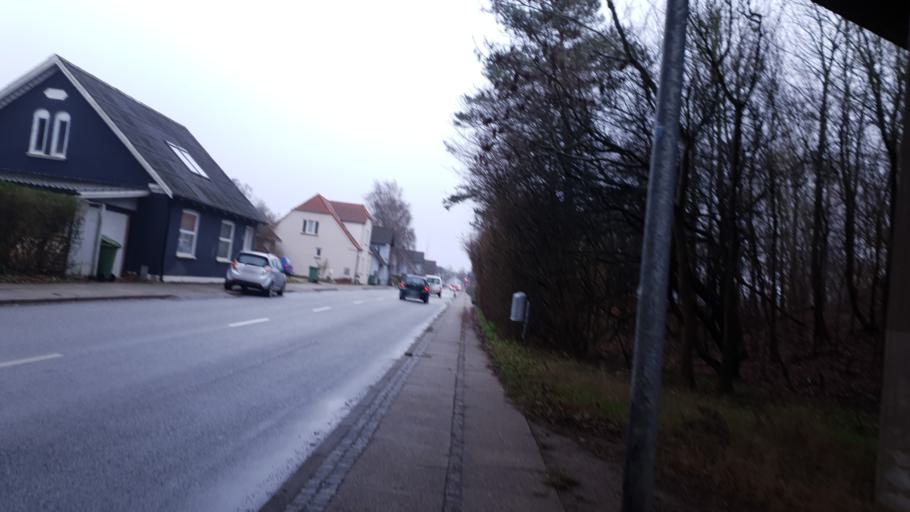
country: DK
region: Central Jutland
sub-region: Hedensted Kommune
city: Hedensted
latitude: 55.7730
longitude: 9.6983
